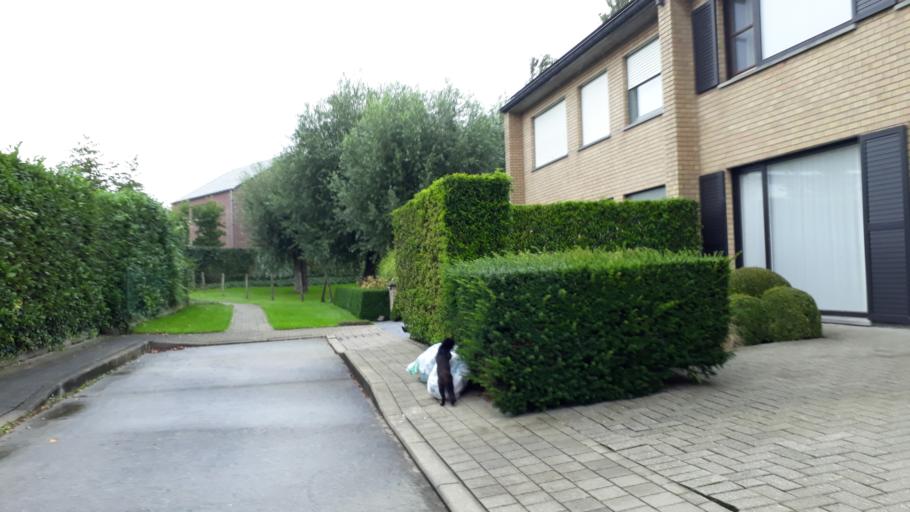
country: BE
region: Flanders
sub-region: Provincie West-Vlaanderen
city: Torhout
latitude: 51.0715
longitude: 3.1142
